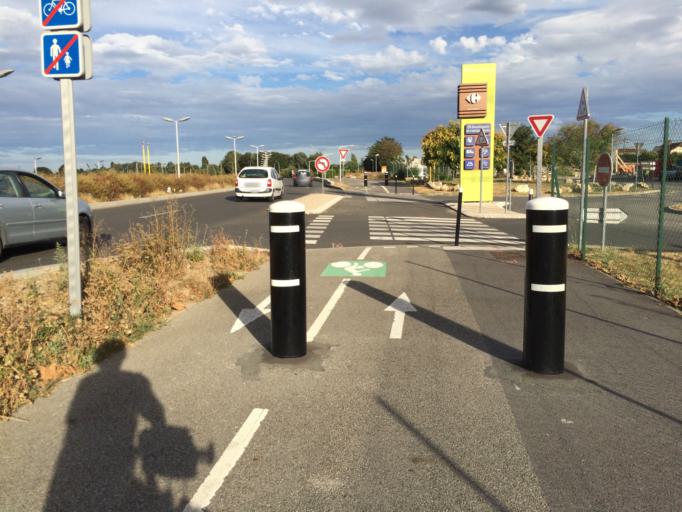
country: FR
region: Ile-de-France
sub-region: Departement de l'Essonne
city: Paray-Vieille-Poste
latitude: 48.7143
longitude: 2.3740
